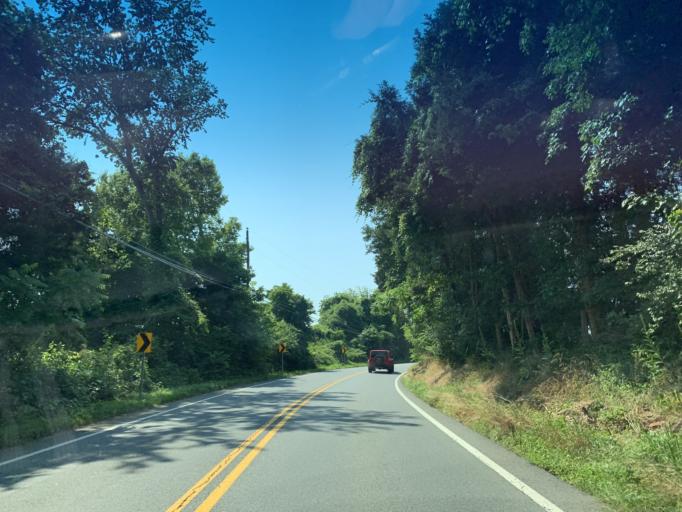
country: US
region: Maryland
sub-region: Montgomery County
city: Poolesville
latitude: 39.1247
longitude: -77.3739
